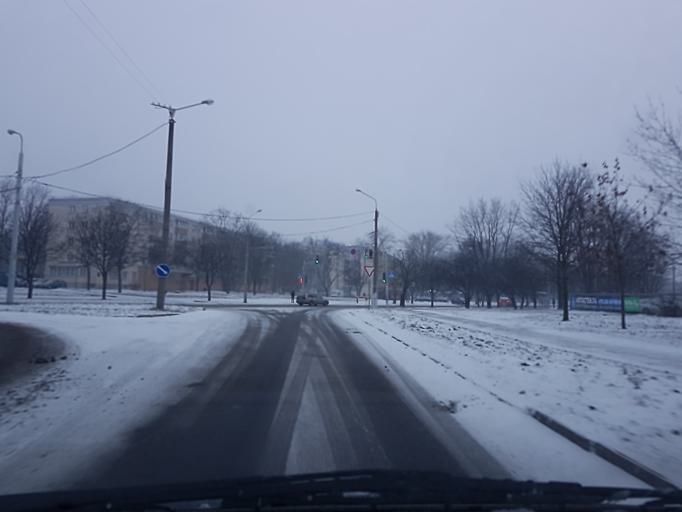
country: BY
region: Minsk
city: Novoye Medvezhino
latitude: 53.8967
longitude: 27.5046
